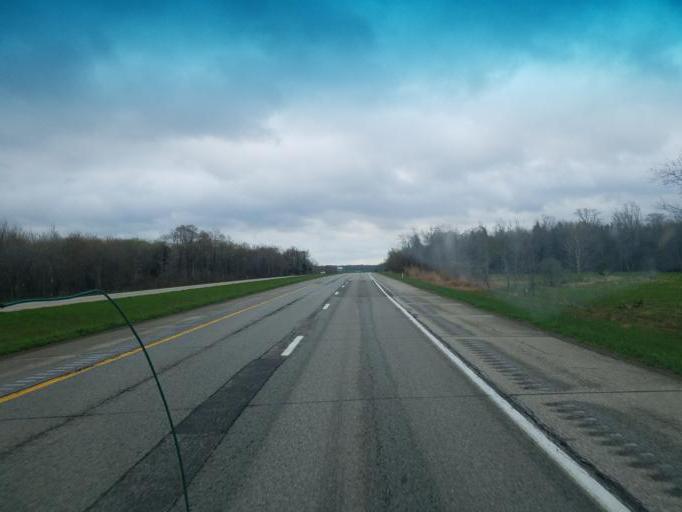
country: US
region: Pennsylvania
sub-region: Erie County
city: North East
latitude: 42.1320
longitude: -79.8115
